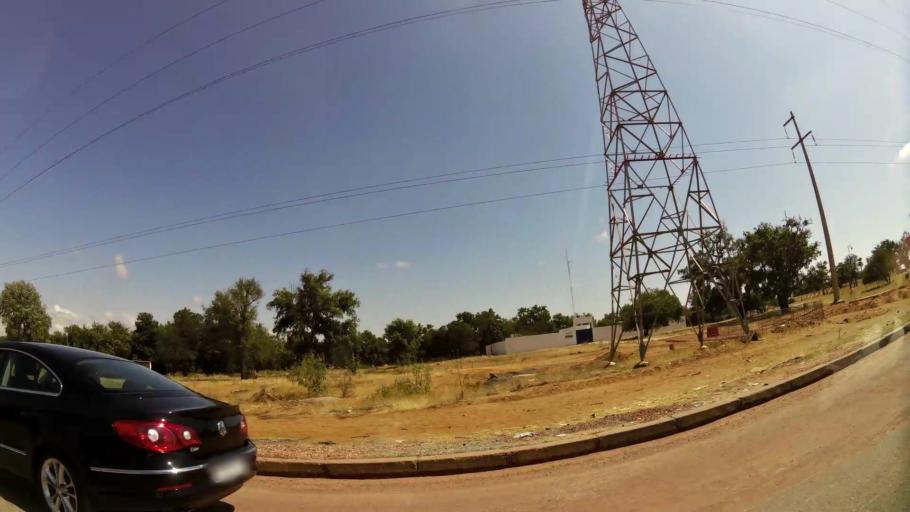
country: MA
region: Gharb-Chrarda-Beni Hssen
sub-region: Kenitra Province
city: Kenitra
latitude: 34.2364
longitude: -6.5704
